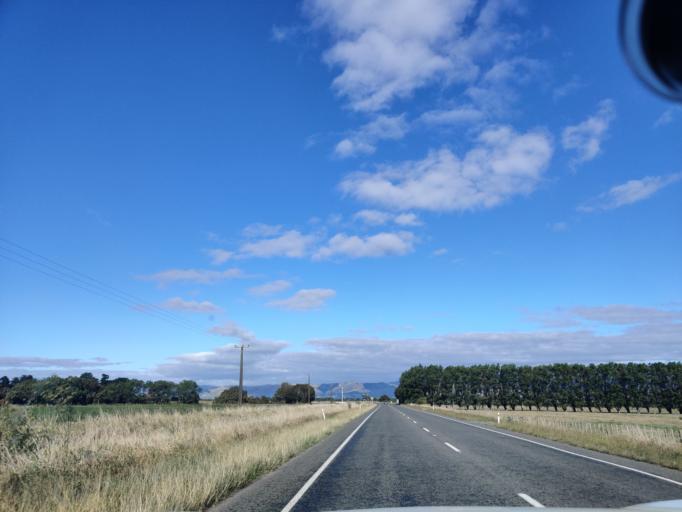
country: NZ
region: Manawatu-Wanganui
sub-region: Horowhenua District
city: Foxton
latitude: -40.4237
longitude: 175.4499
